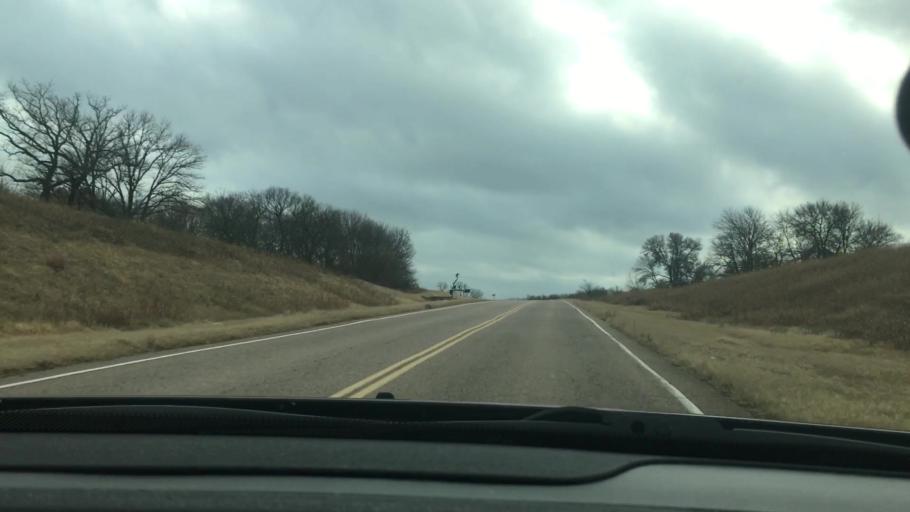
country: US
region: Oklahoma
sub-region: Bryan County
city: Durant
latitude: 34.0829
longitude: -96.3790
